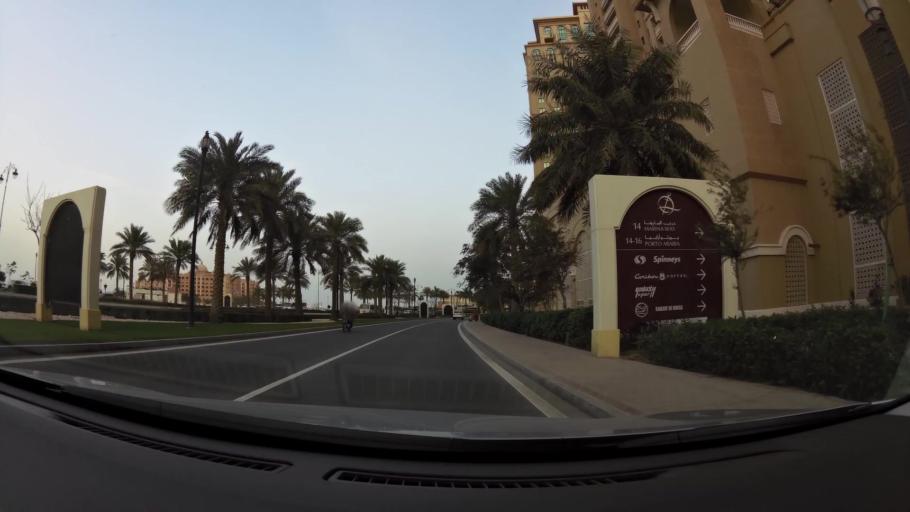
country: QA
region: Baladiyat ad Dawhah
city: Doha
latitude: 25.3744
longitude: 51.5449
